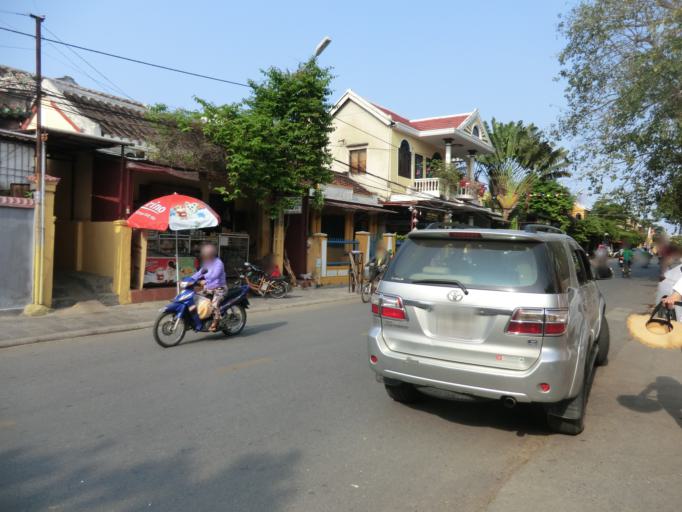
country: VN
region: Quang Nam
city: Hoi An
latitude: 15.8784
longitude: 108.3274
